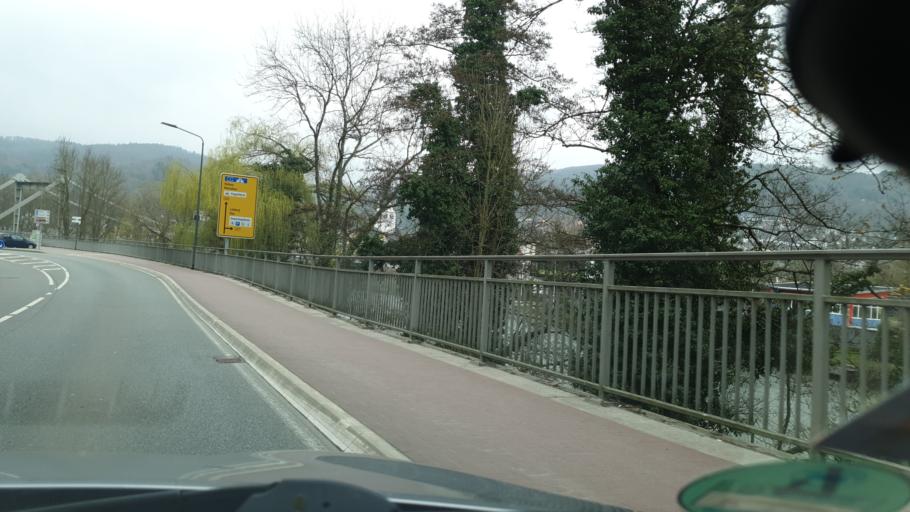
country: DE
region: Rheinland-Pfalz
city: Nassau
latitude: 50.3102
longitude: 7.7958
